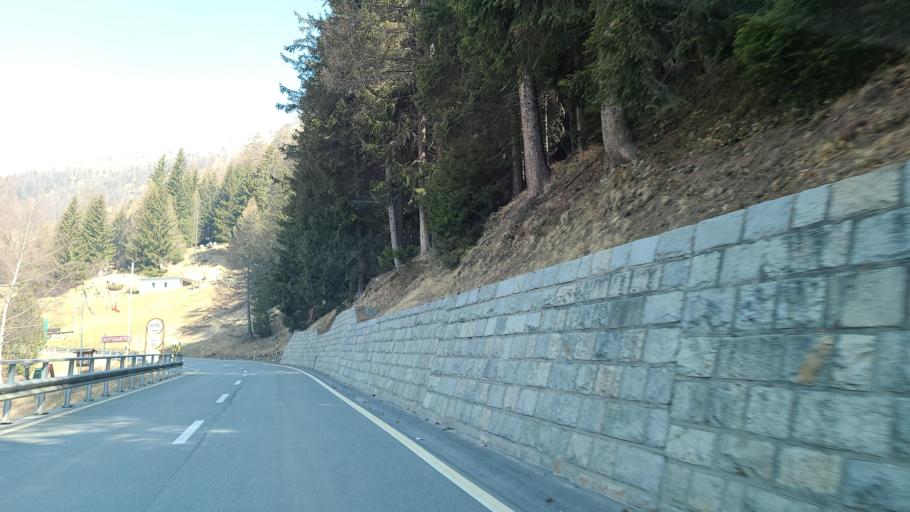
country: CH
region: Grisons
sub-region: Bernina District
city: Poschiavo
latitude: 46.3885
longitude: 10.0803
